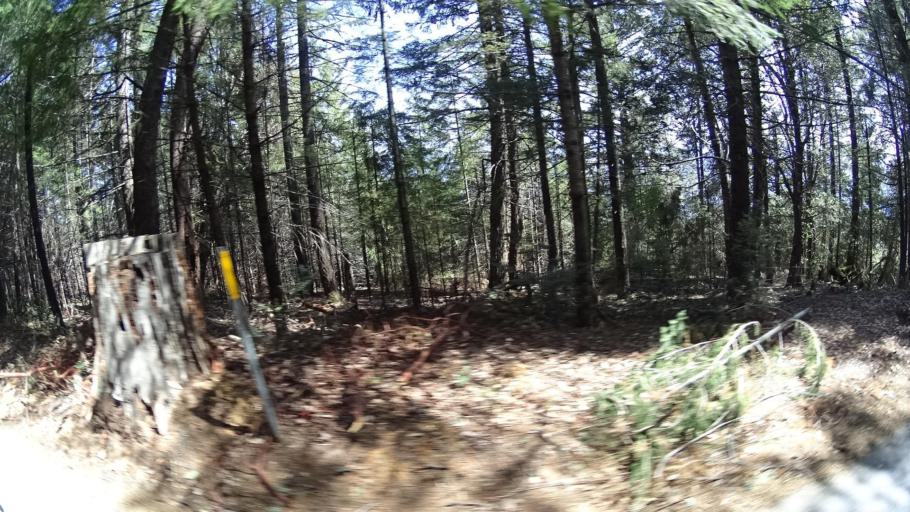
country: US
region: California
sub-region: Humboldt County
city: Redway
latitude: 40.0933
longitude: -123.6775
